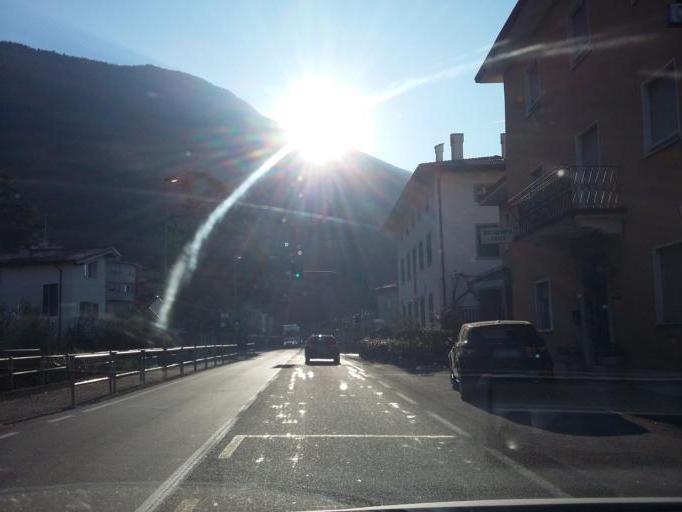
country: IT
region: Trentino-Alto Adige
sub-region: Provincia di Trento
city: Bolognano-Vignole
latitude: 45.9093
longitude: 10.9014
